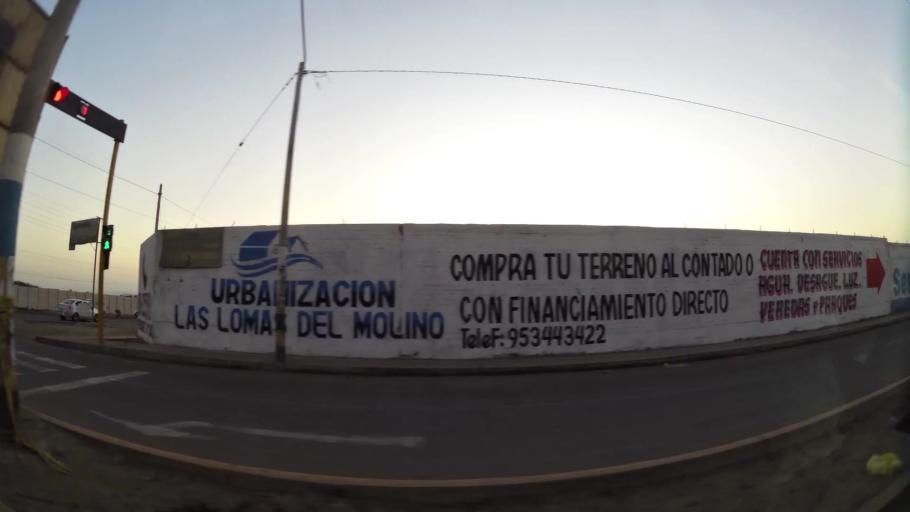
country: PE
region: Ica
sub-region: Provincia de Pisco
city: Pisco
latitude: -13.7096
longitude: -76.1849
